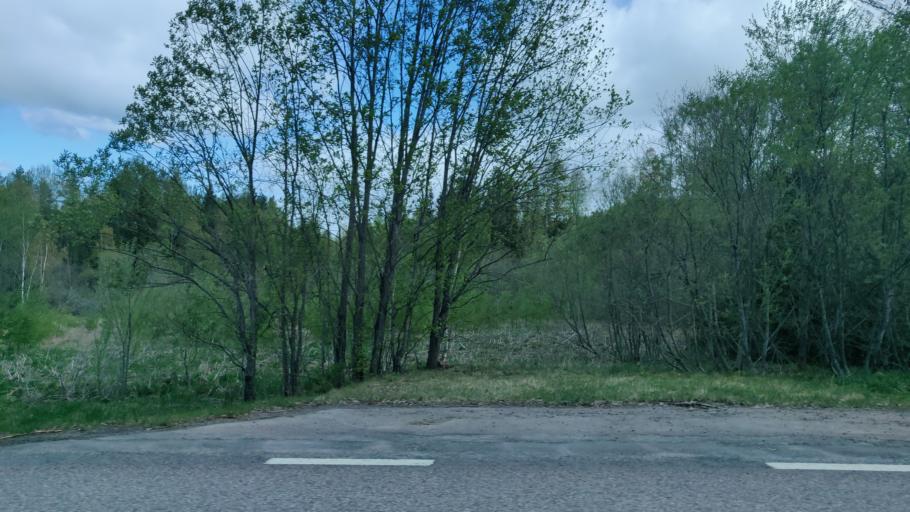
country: SE
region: Vaermland
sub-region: Karlstads Kommun
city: Molkom
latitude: 59.6137
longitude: 13.7319
